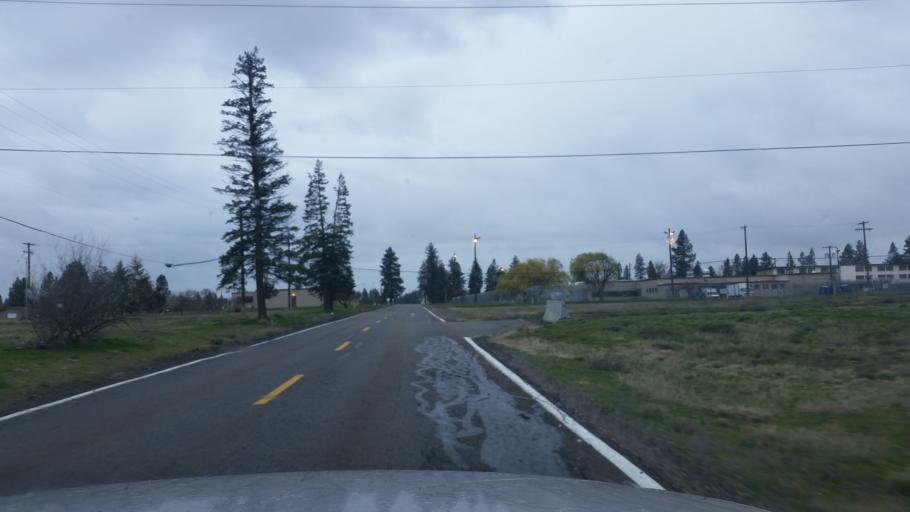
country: US
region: Washington
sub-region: Spokane County
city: Airway Heights
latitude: 47.6237
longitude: -117.5133
